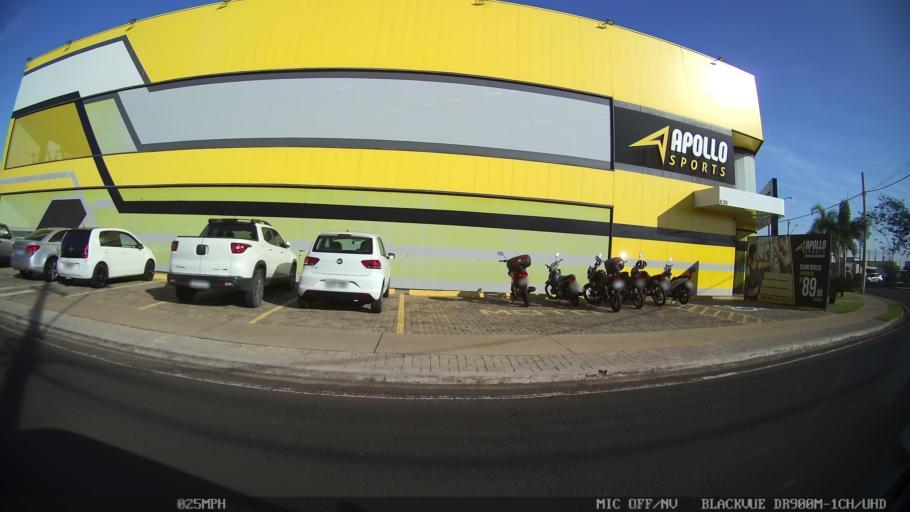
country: BR
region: Sao Paulo
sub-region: Sao Jose Do Rio Preto
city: Sao Jose do Rio Preto
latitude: -20.7781
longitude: -49.3422
